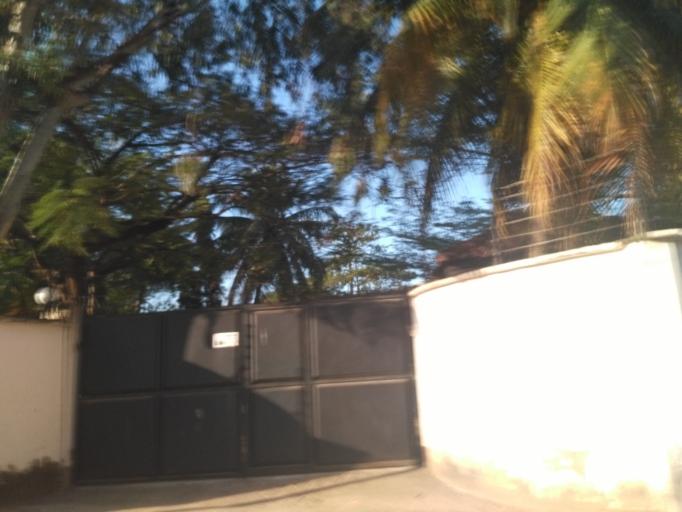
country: TZ
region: Dar es Salaam
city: Magomeni
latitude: -6.7608
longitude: 39.2562
